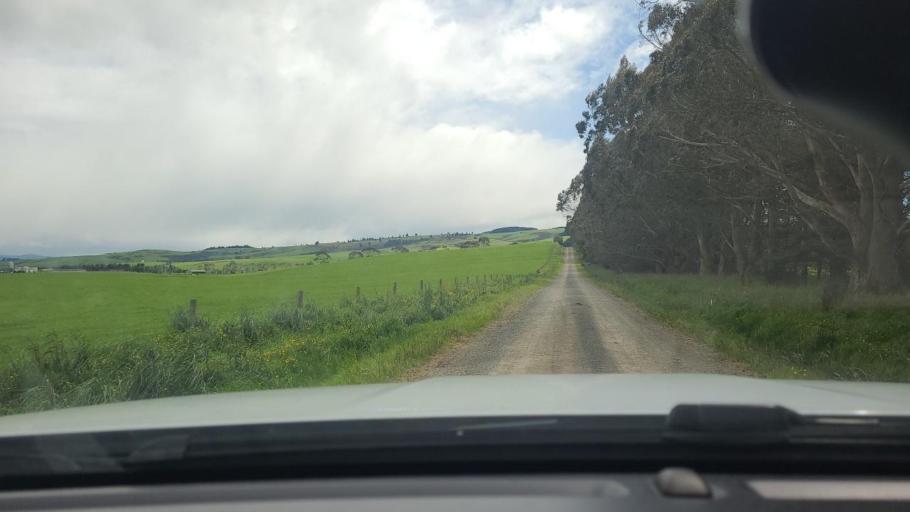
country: NZ
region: Southland
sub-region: Southland District
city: Winton
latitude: -46.0067
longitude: 168.2100
